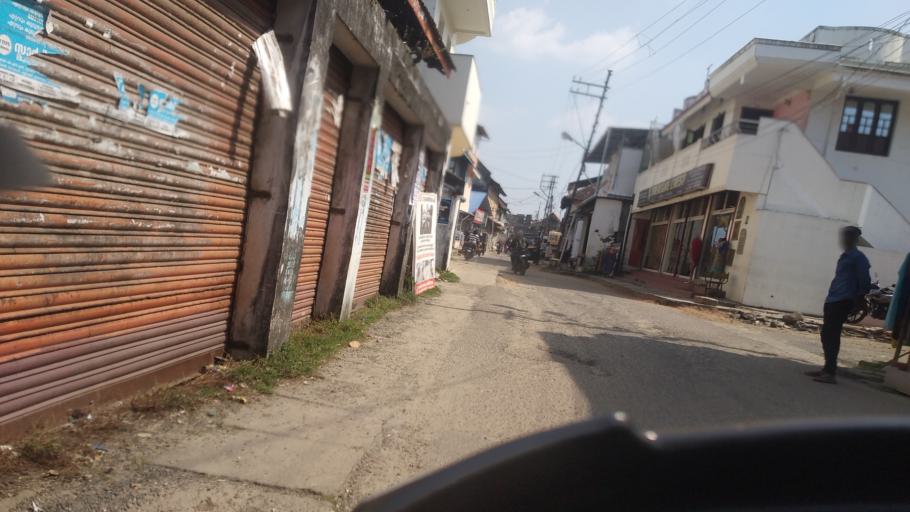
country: IN
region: Kerala
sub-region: Ernakulam
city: Cochin
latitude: 9.9667
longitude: 76.2531
